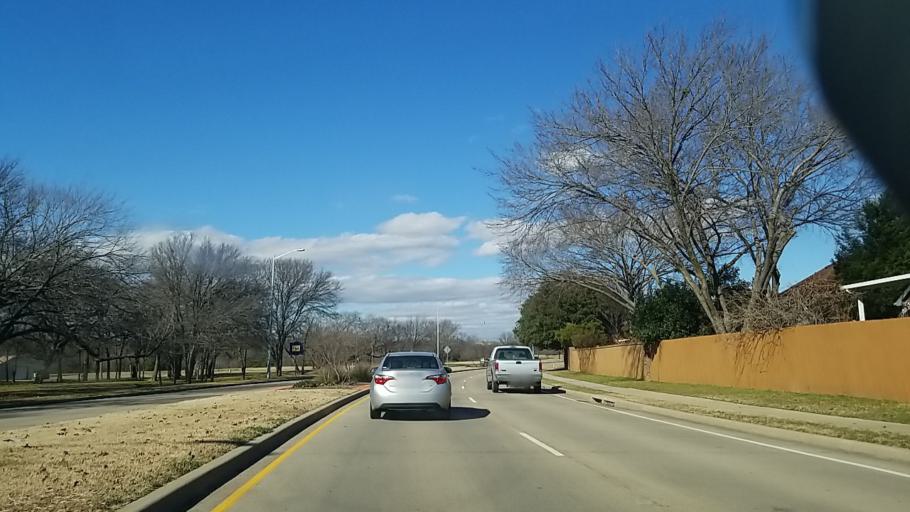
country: US
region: Texas
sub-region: Denton County
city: Denton
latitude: 33.1768
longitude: -97.1232
